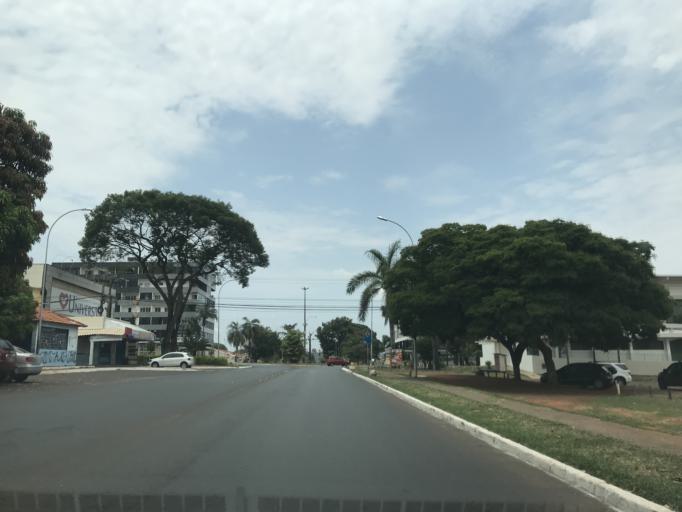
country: BR
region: Federal District
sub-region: Brasilia
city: Brasilia
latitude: -15.6466
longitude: -47.8031
